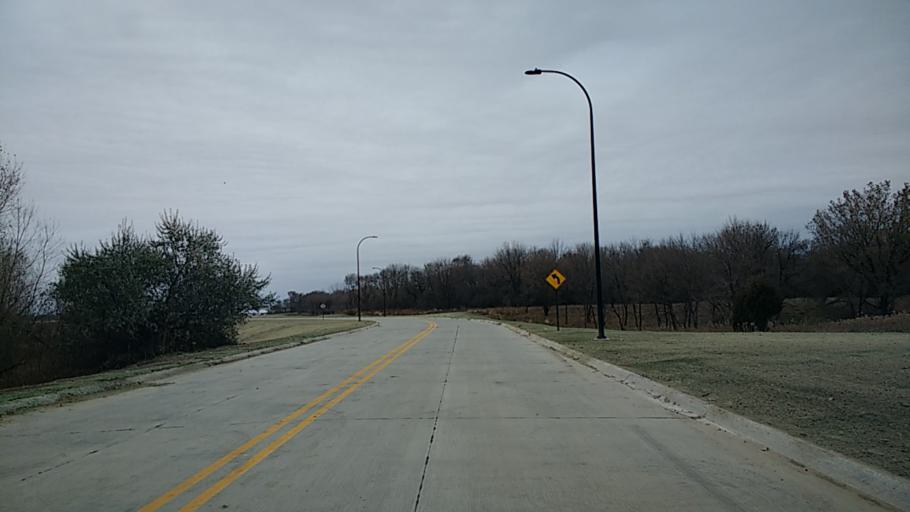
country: US
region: Iowa
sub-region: Woodbury County
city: Sergeant Bluff
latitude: 42.4182
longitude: -96.3772
